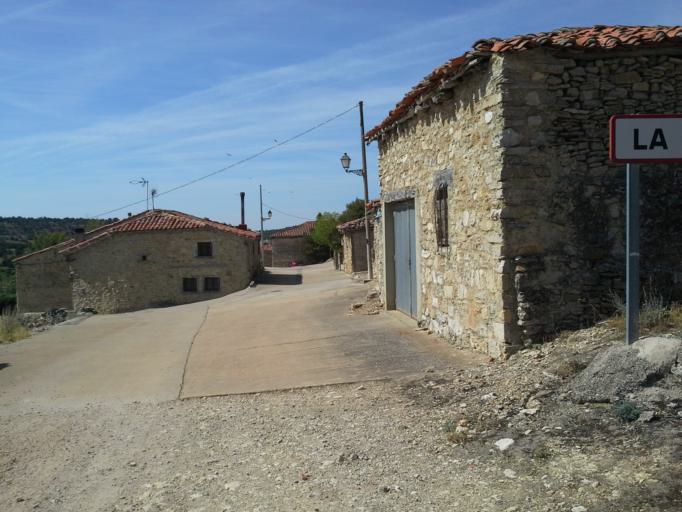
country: ES
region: Castille and Leon
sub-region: Provincia de Soria
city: Abejar
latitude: 41.7390
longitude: -2.7394
